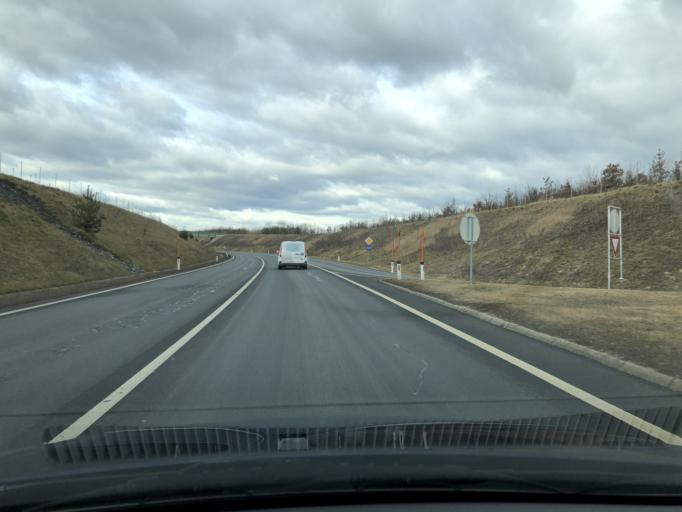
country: AT
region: Burgenland
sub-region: Politischer Bezirk Oberwart
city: Schachendorf
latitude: 47.2758
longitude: 16.4414
